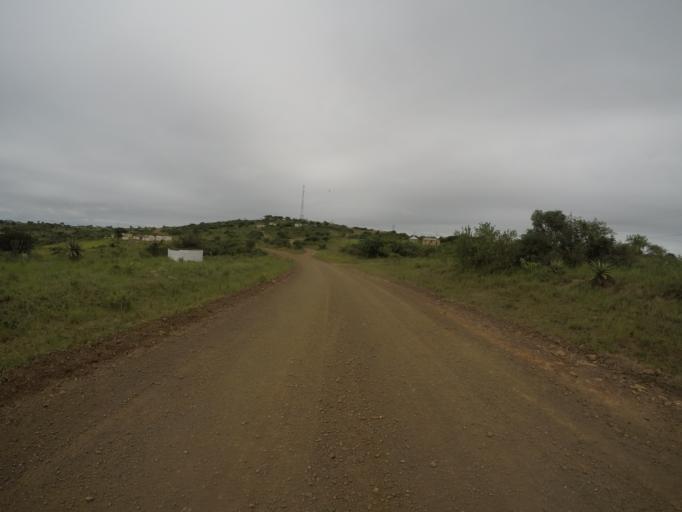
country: ZA
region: KwaZulu-Natal
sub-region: uThungulu District Municipality
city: Empangeni
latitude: -28.6030
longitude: 31.8399
